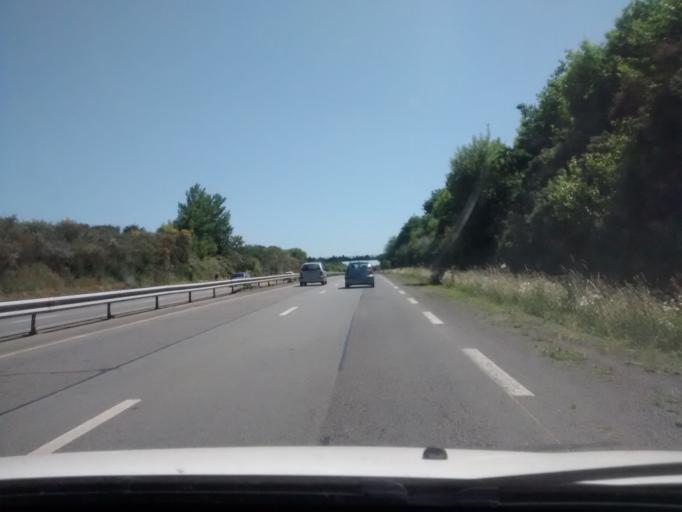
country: FR
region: Brittany
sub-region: Departement d'Ille-et-Vilaine
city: Miniac-Morvan
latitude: 48.5003
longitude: -1.9080
